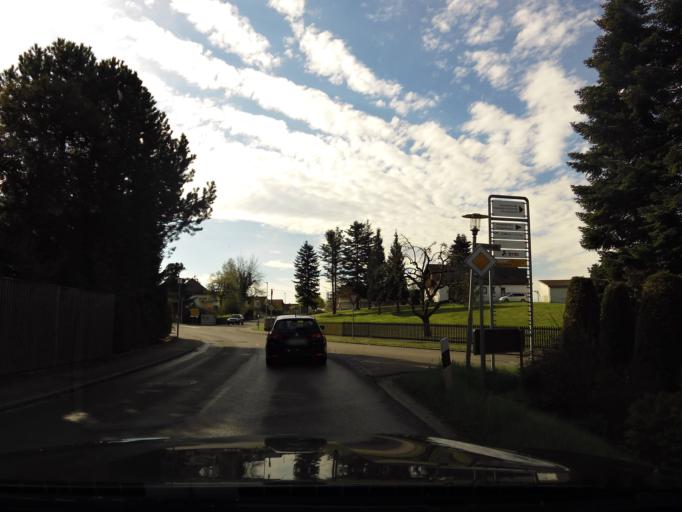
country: DE
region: Bavaria
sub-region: Upper Bavaria
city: Oberding
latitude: 48.3376
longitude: 11.8403
